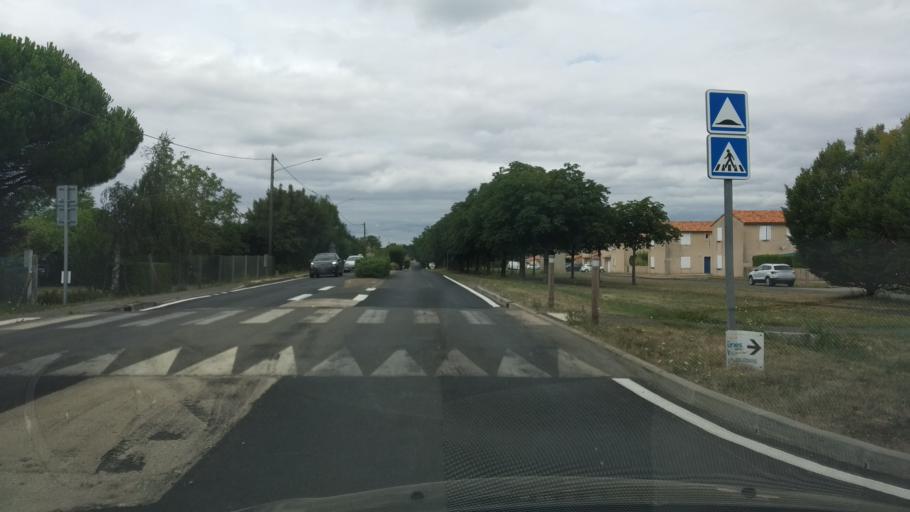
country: FR
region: Poitou-Charentes
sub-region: Departement de la Vienne
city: Roches-Premarie-Andille
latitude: 46.4769
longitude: 0.3692
